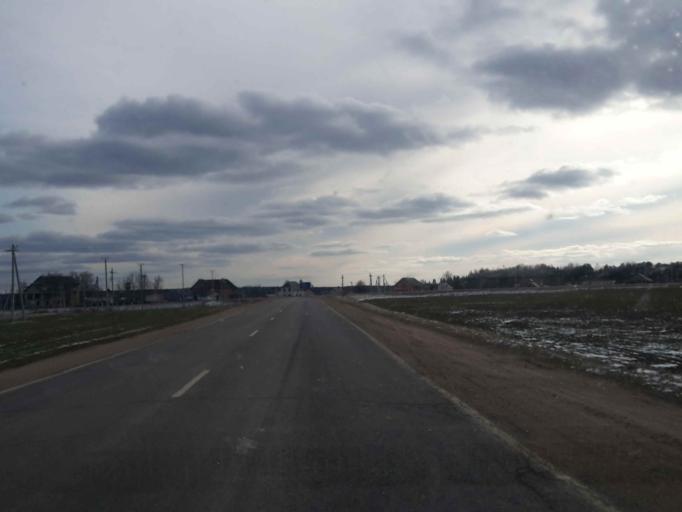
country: BY
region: Minsk
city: Il'ya
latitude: 54.5127
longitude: 27.2224
